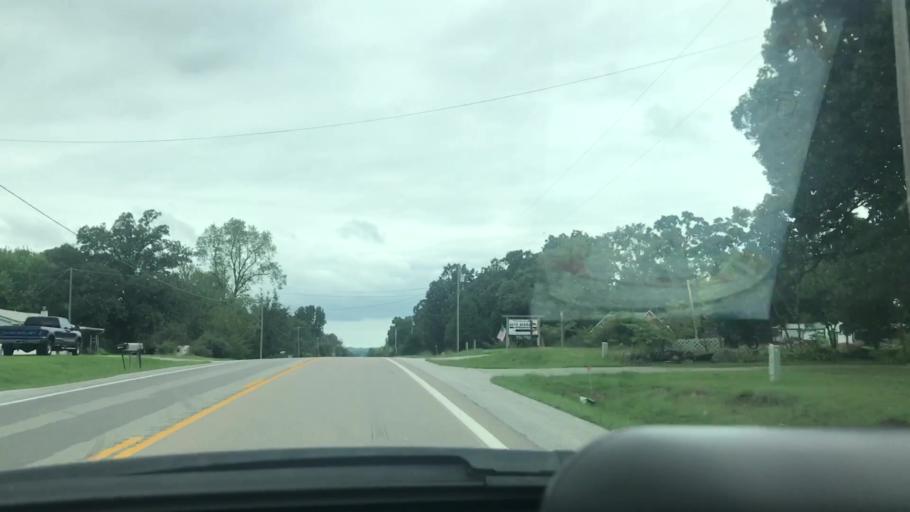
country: US
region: Missouri
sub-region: Dallas County
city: Buffalo
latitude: 37.7027
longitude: -93.1085
